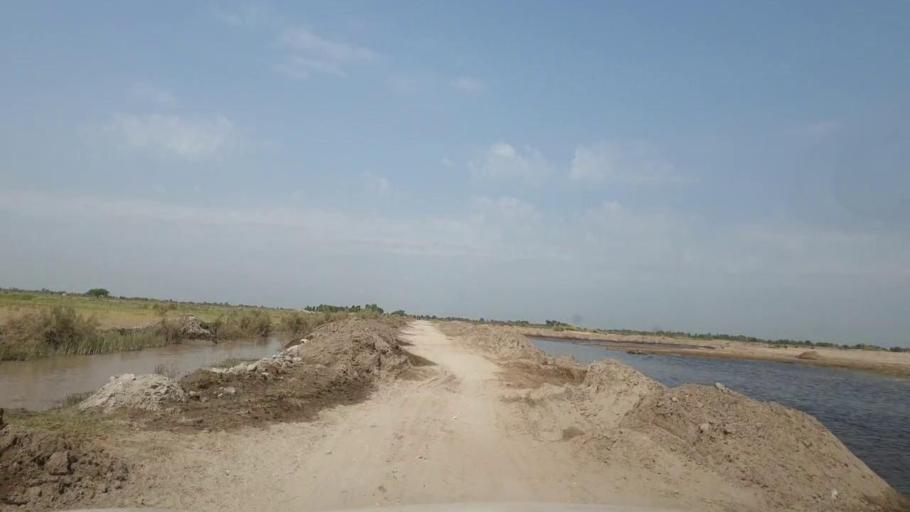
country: PK
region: Sindh
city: Ratodero
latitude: 27.8388
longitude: 68.2562
